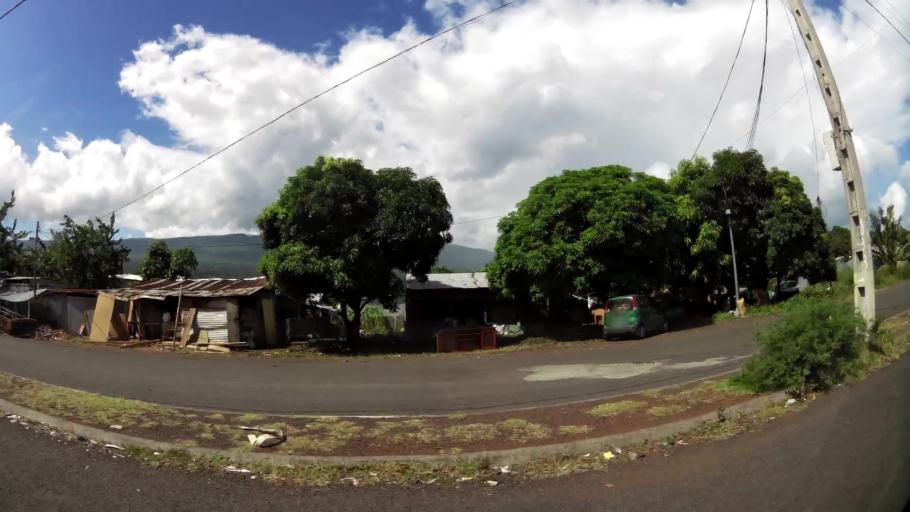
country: KM
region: Grande Comore
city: Mavingouni
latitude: -11.7272
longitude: 43.2441
